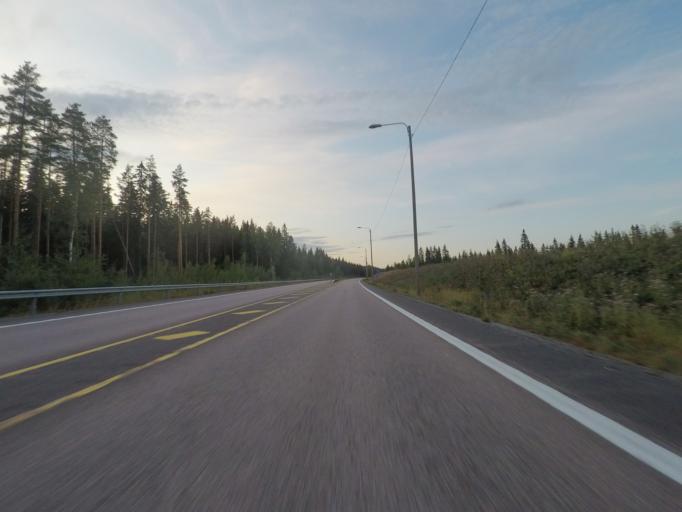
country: FI
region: Central Finland
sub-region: Jyvaeskylae
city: Saeynaetsalo
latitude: 62.1530
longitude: 25.8962
